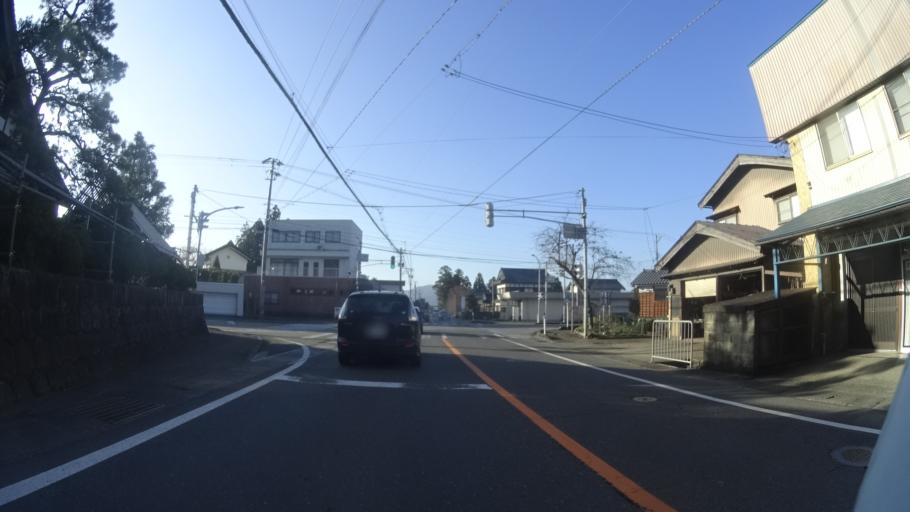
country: JP
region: Fukui
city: Ono
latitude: 35.9739
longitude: 136.5477
